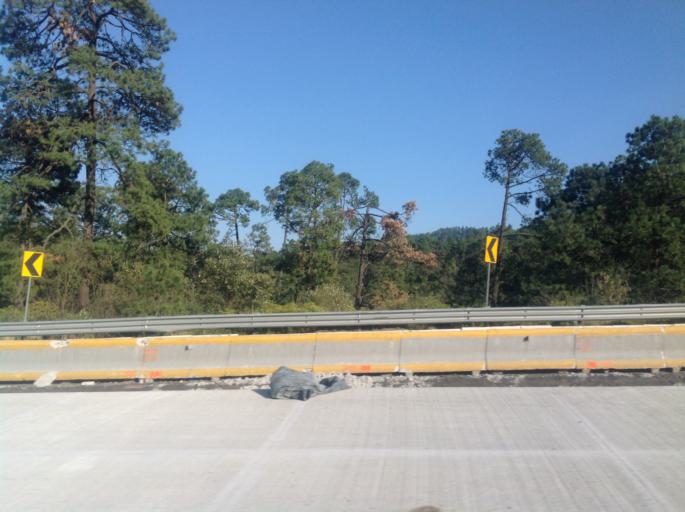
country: MX
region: Mexico
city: Rio Frio de Juarez
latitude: 19.3341
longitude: -98.6837
